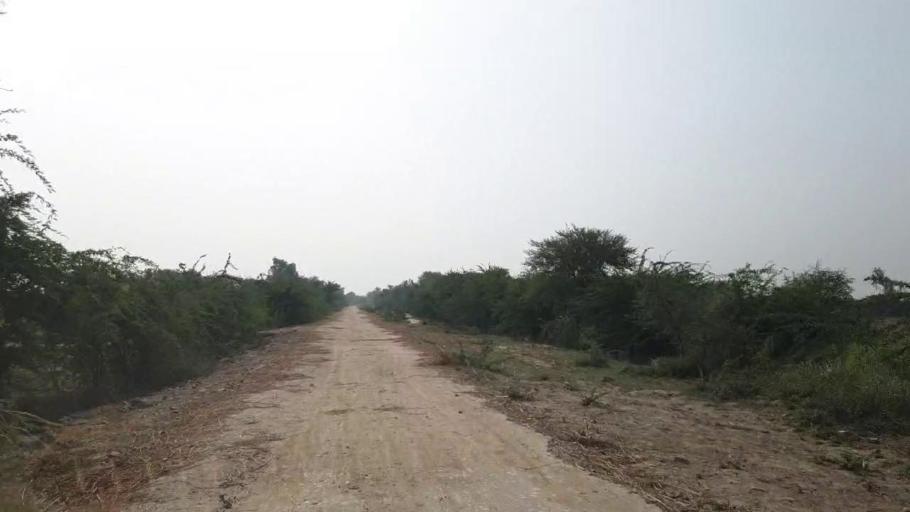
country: PK
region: Sindh
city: Kario
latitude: 24.7592
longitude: 68.5637
